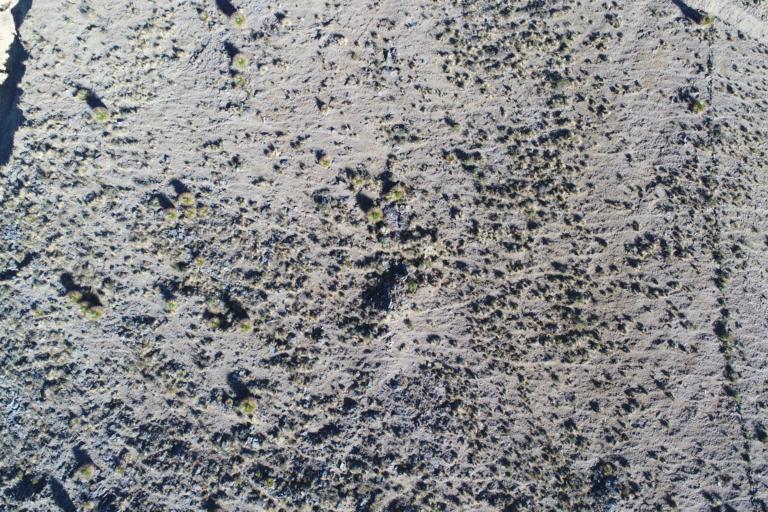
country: BO
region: La Paz
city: Viloco
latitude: -16.8119
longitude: -67.5507
